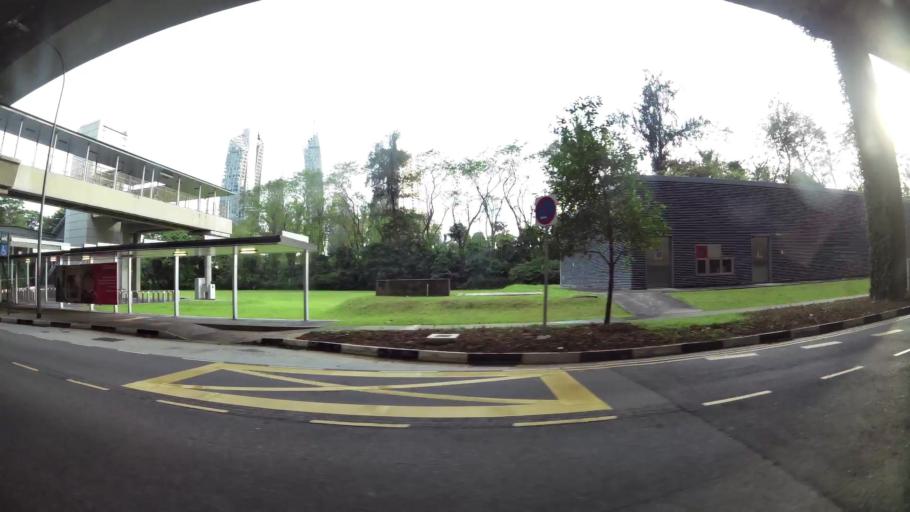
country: SG
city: Singapore
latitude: 1.2709
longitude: 103.8095
